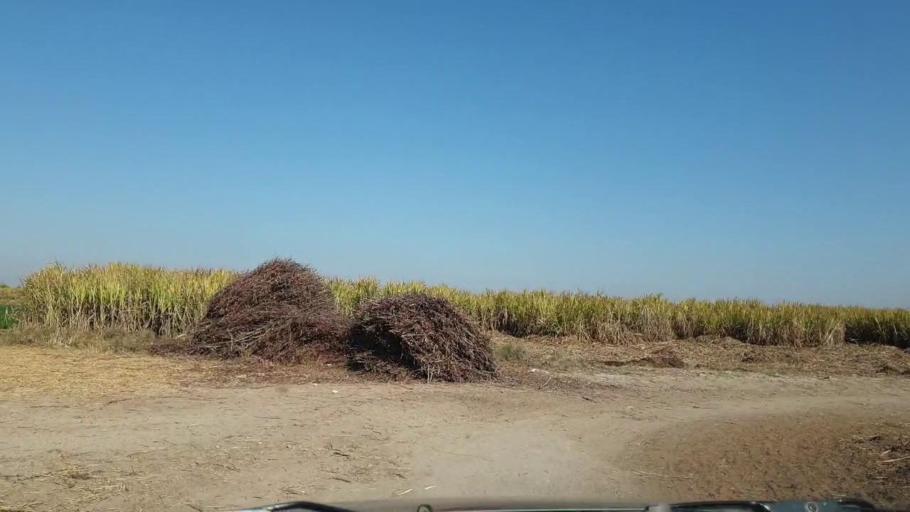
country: PK
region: Sindh
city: Sinjhoro
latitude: 26.1109
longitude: 68.8439
